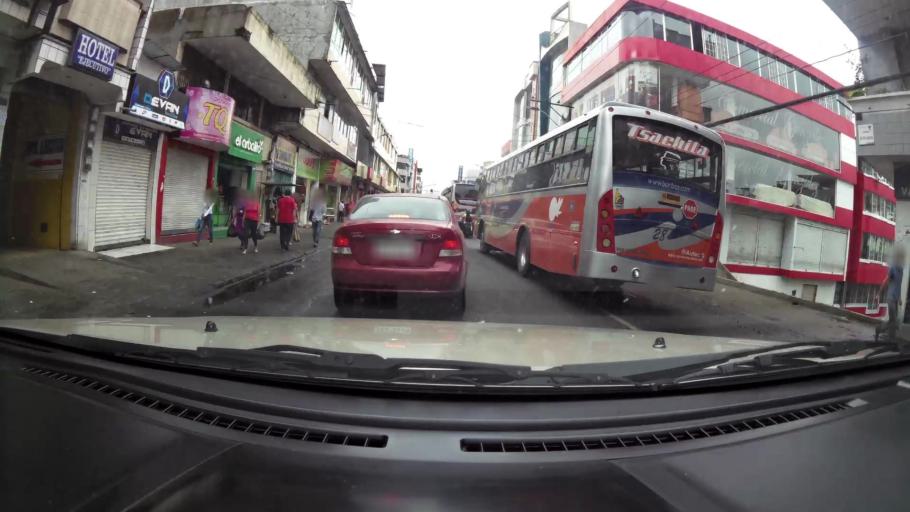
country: EC
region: Santo Domingo de los Tsachilas
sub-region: Canton Santo Domingo de los Colorados
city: Santo Domingo de los Colorados
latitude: -0.2534
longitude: -79.1725
